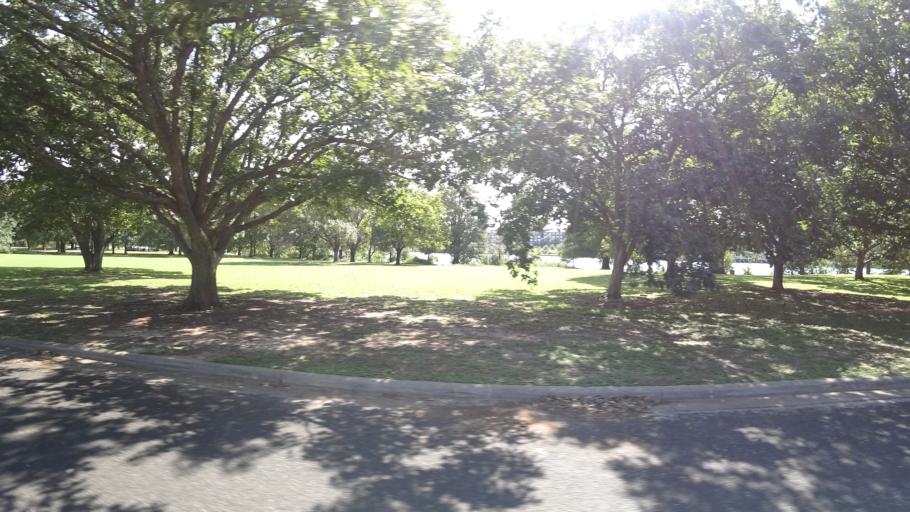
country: US
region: Texas
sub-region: Travis County
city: Austin
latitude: 30.2496
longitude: -97.7297
